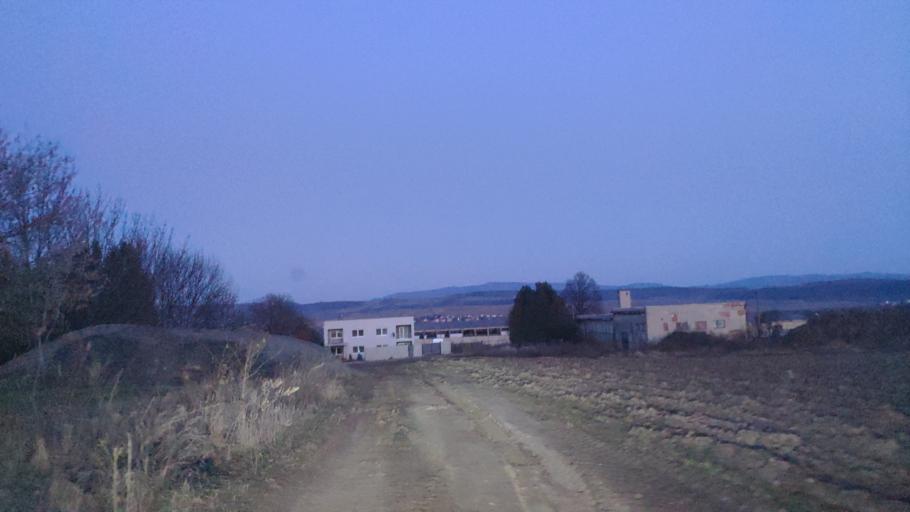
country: SK
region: Kosicky
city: Kosice
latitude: 48.8253
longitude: 21.2911
